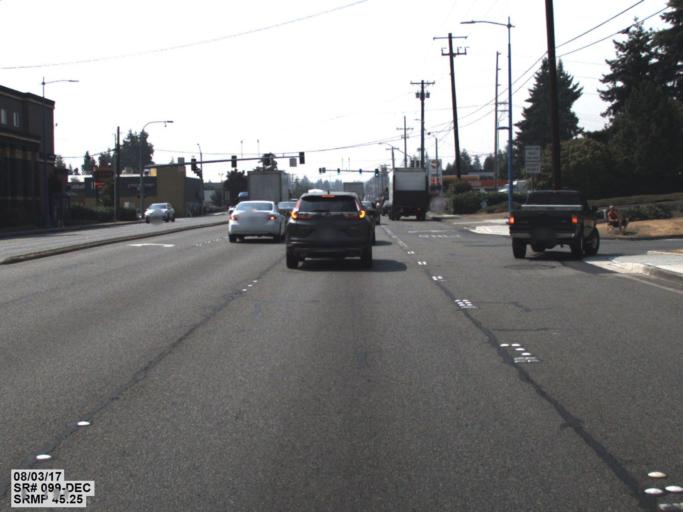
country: US
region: Washington
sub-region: Snohomish County
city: Mountlake Terrace
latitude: 47.8008
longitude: -122.3309
